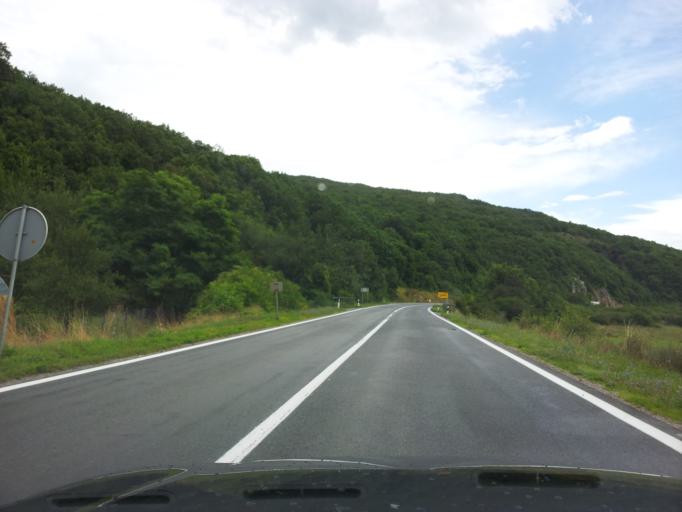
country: BA
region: Federation of Bosnia and Herzegovina
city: Bihac
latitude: 44.6349
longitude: 15.7264
